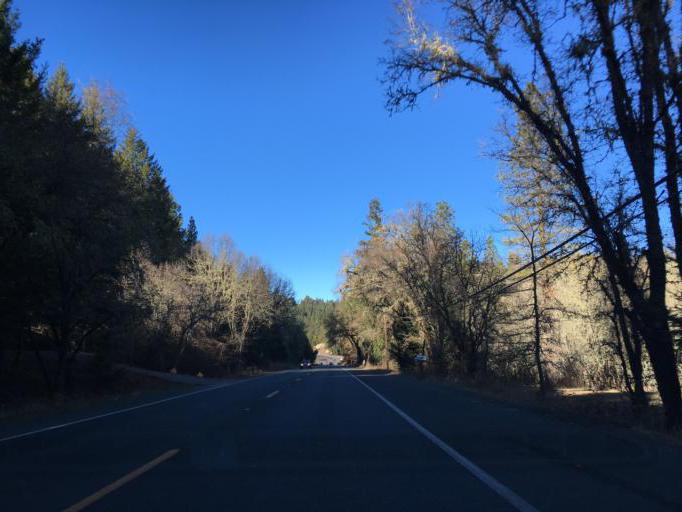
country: US
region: California
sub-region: Mendocino County
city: Brooktrails
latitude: 39.4593
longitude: -123.3494
